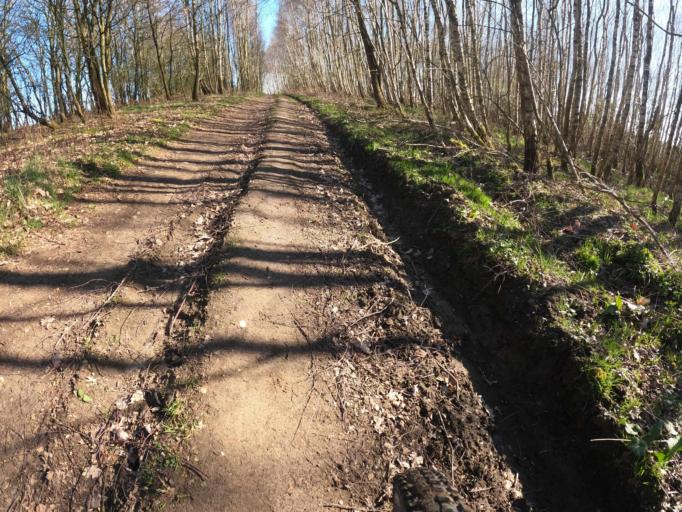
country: PL
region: West Pomeranian Voivodeship
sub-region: Powiat kolobrzeski
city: Ryman
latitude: 54.0106
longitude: 15.4810
